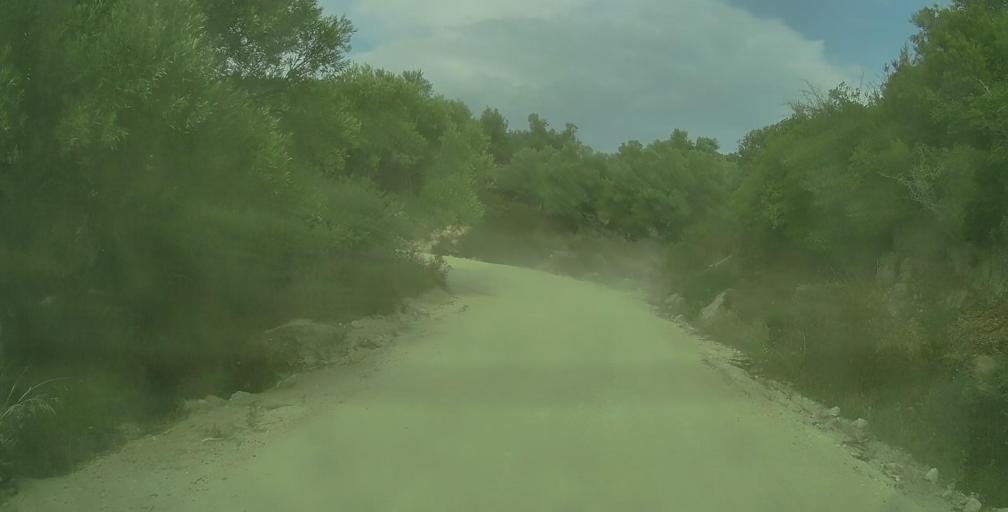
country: GR
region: Central Macedonia
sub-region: Nomos Chalkidikis
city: Sykia
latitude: 39.9933
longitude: 23.9171
